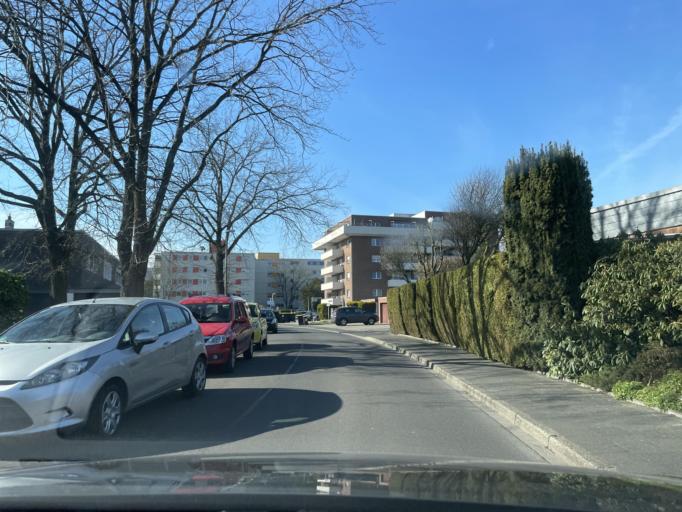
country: DE
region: North Rhine-Westphalia
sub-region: Regierungsbezirk Dusseldorf
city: Viersen
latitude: 51.2012
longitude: 6.3818
